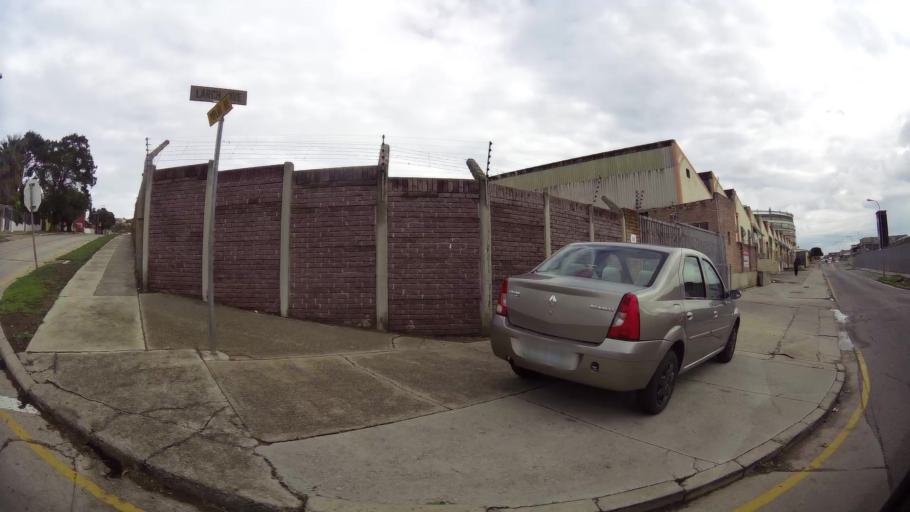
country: ZA
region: Eastern Cape
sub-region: Nelson Mandela Bay Metropolitan Municipality
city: Port Elizabeth
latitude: -33.9372
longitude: 25.5854
